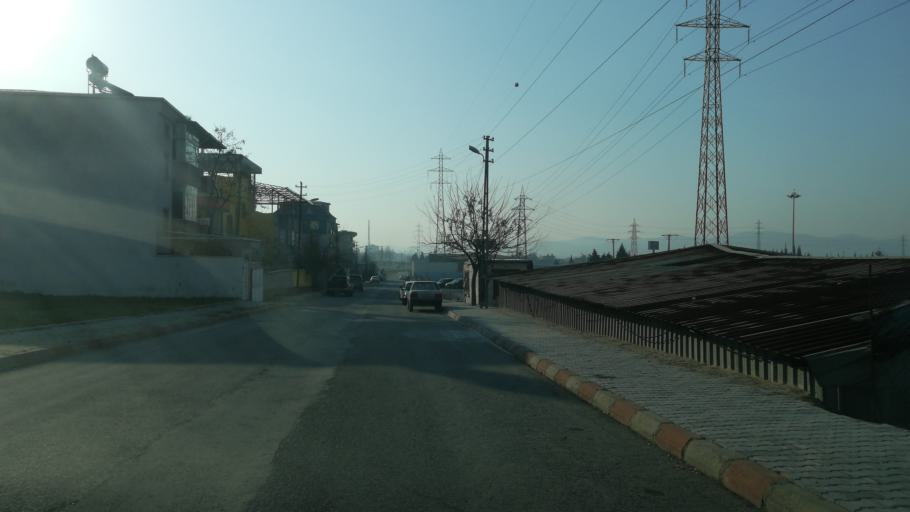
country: TR
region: Kahramanmaras
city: Kahramanmaras
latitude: 37.5650
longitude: 36.9449
